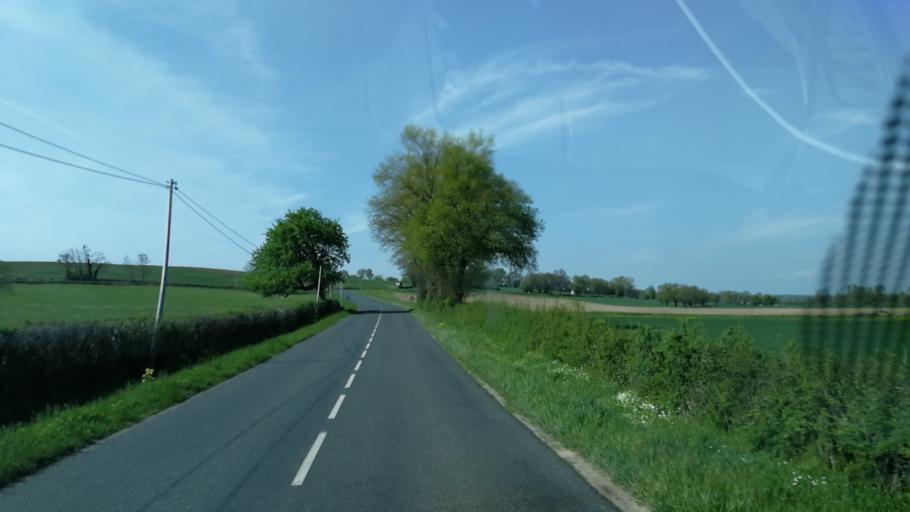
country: FR
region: Auvergne
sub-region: Departement de l'Allier
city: Saint-Gerand-le-Puy
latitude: 46.3552
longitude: 3.5783
